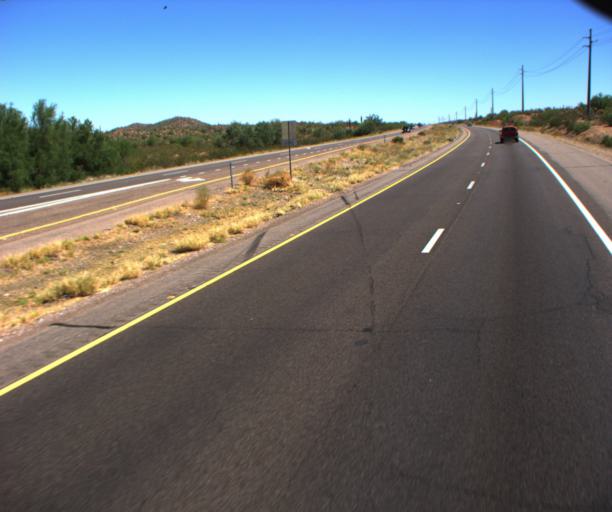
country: US
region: Arizona
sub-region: Maricopa County
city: Fountain Hills
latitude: 33.5376
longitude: -111.7254
